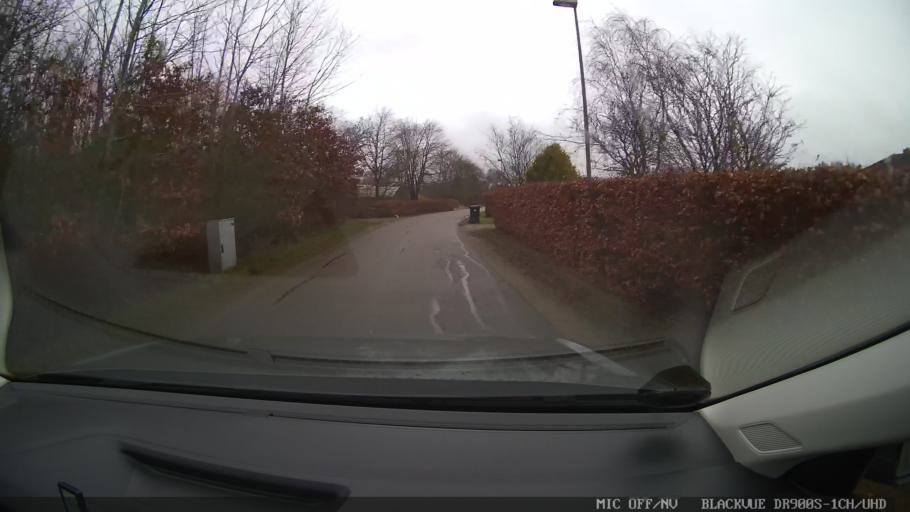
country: DK
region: Central Jutland
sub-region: Viborg Kommune
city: Karup
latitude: 56.3212
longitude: 9.2581
